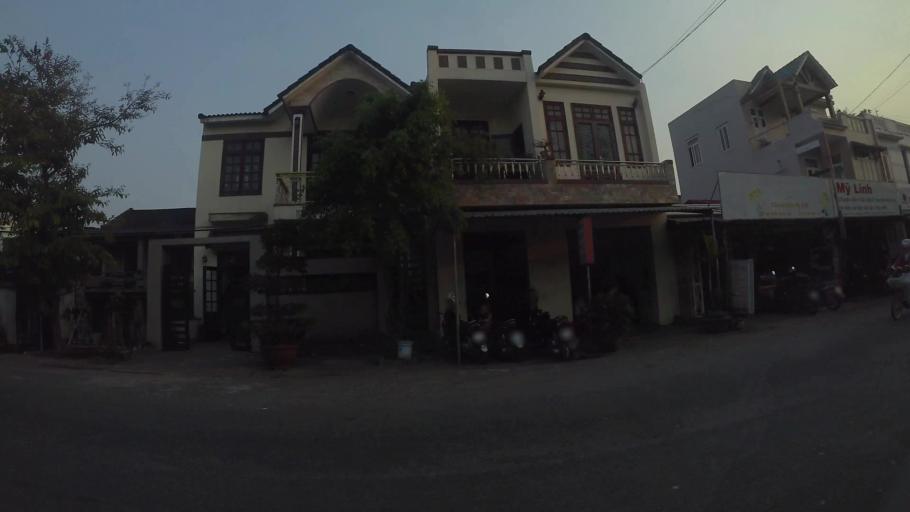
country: VN
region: Quang Nam
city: Quang Nam
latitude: 15.9471
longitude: 108.2208
